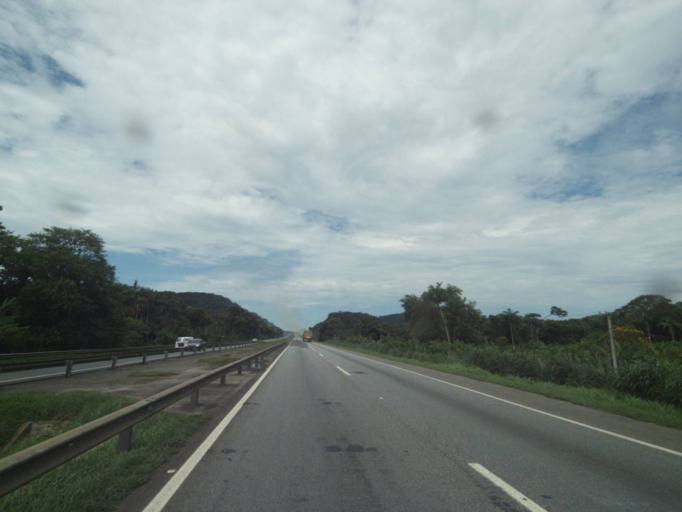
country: BR
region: Parana
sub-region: Antonina
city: Antonina
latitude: -25.5366
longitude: -48.7657
